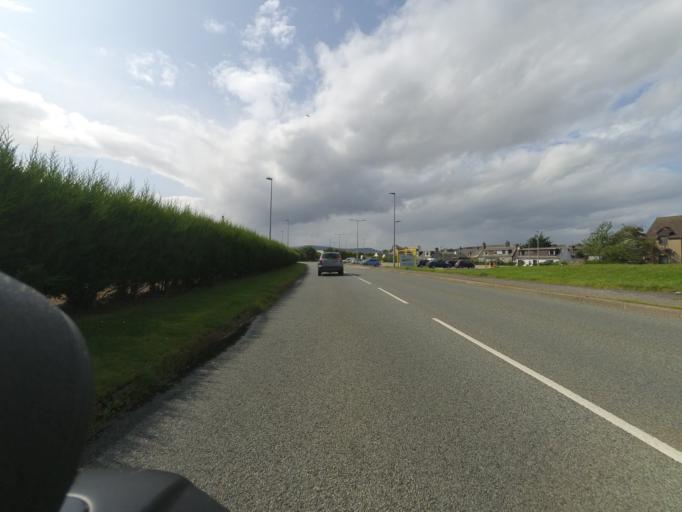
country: GB
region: Scotland
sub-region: Highland
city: Invergordon
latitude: 57.6870
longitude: -4.1724
